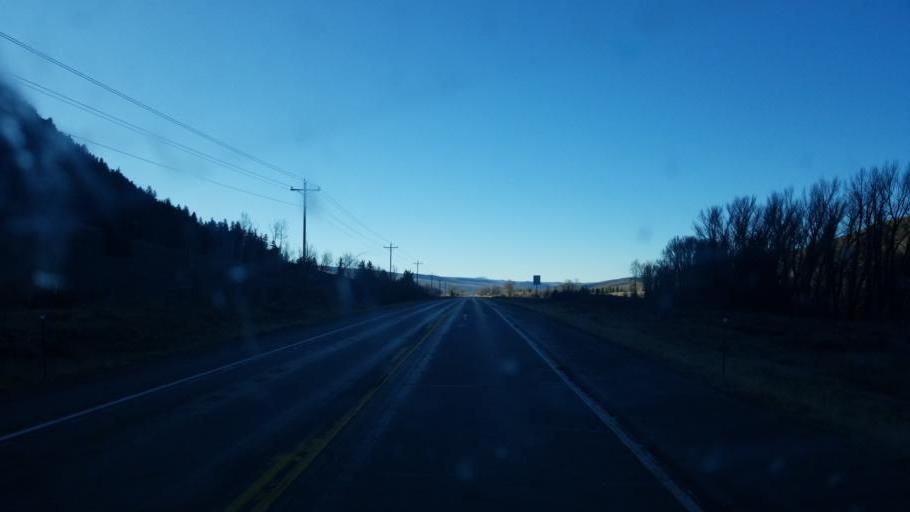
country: US
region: Colorado
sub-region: Gunnison County
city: Crested Butte
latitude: 38.7804
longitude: -106.8700
